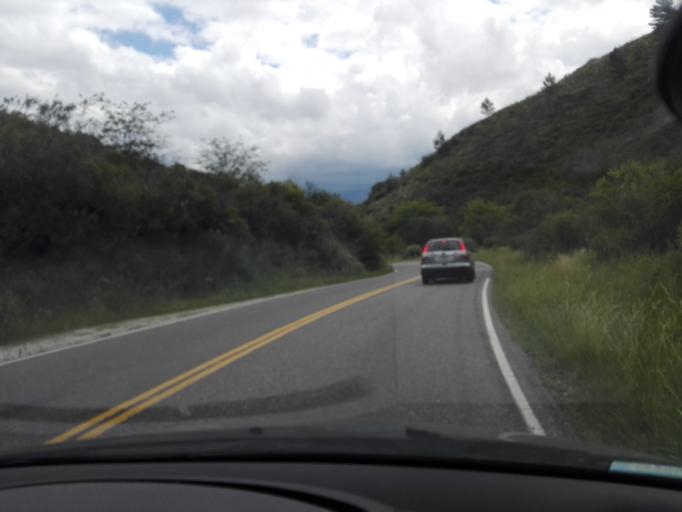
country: AR
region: Cordoba
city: Cuesta Blanca
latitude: -31.6036
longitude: -64.5514
